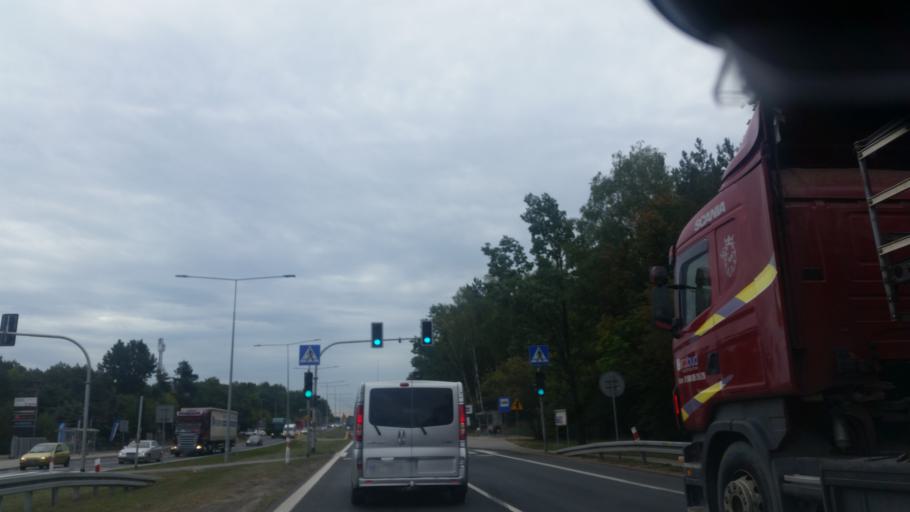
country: PL
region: Masovian Voivodeship
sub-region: Powiat warszawski zachodni
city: Lomianki
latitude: 52.3233
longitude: 20.9110
